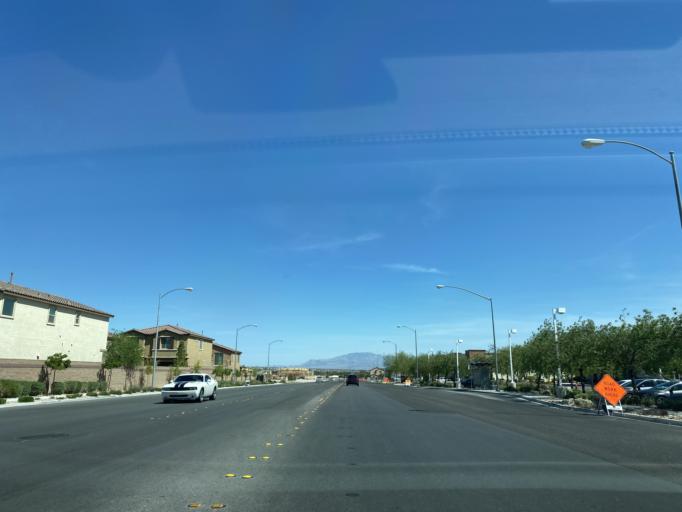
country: US
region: Nevada
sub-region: Clark County
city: Spring Valley
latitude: 36.0781
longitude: -115.2608
